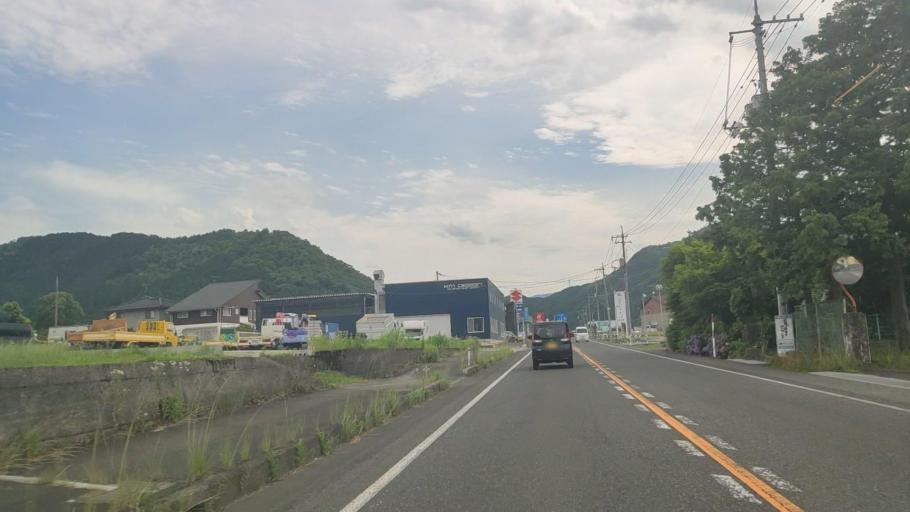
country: JP
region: Tottori
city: Tottori
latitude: 35.3579
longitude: 134.2087
